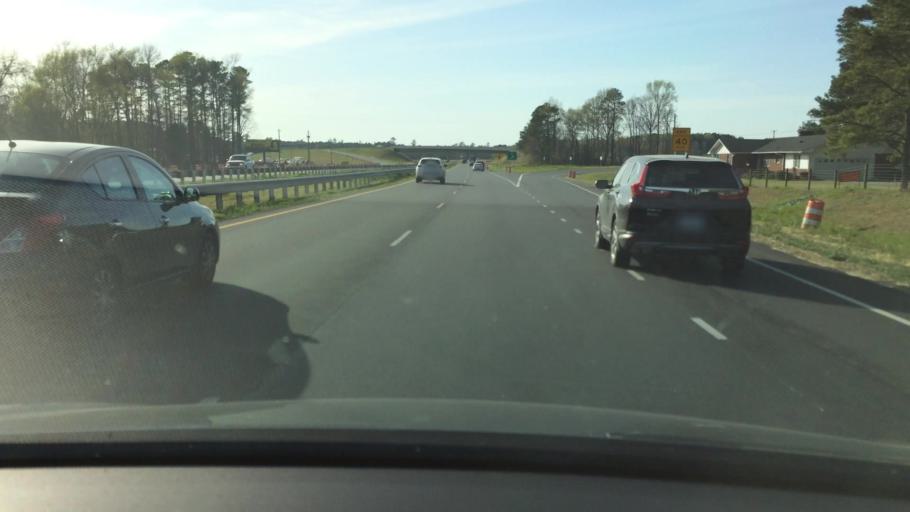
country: US
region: North Carolina
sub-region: Johnston County
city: Pine Level
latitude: 35.4896
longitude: -78.2658
